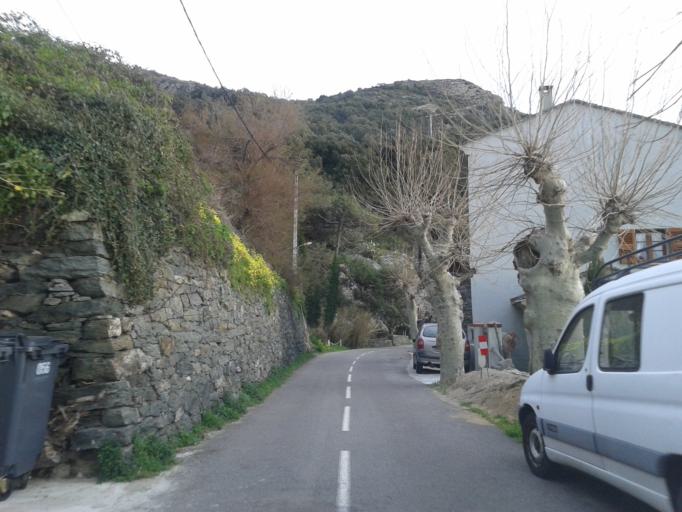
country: FR
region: Corsica
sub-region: Departement de la Haute-Corse
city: Brando
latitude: 42.8873
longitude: 9.3349
